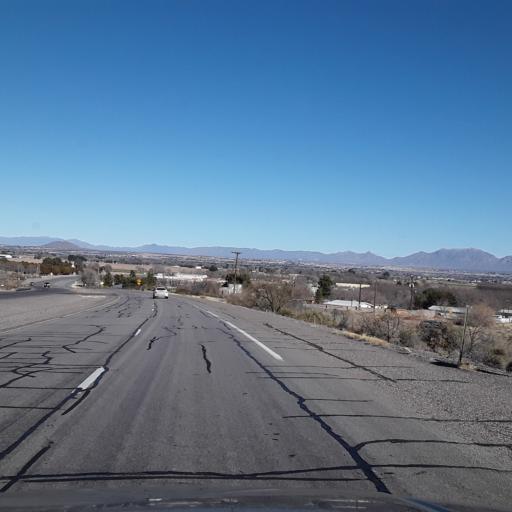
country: US
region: New Mexico
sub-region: Dona Ana County
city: Mesilla
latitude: 32.2954
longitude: -106.8578
